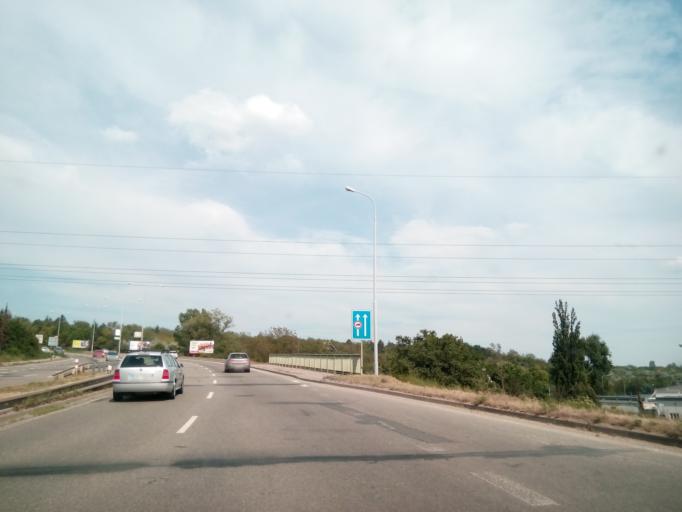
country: CZ
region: South Moravian
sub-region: Mesto Brno
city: Brno
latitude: 49.1750
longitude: 16.6405
